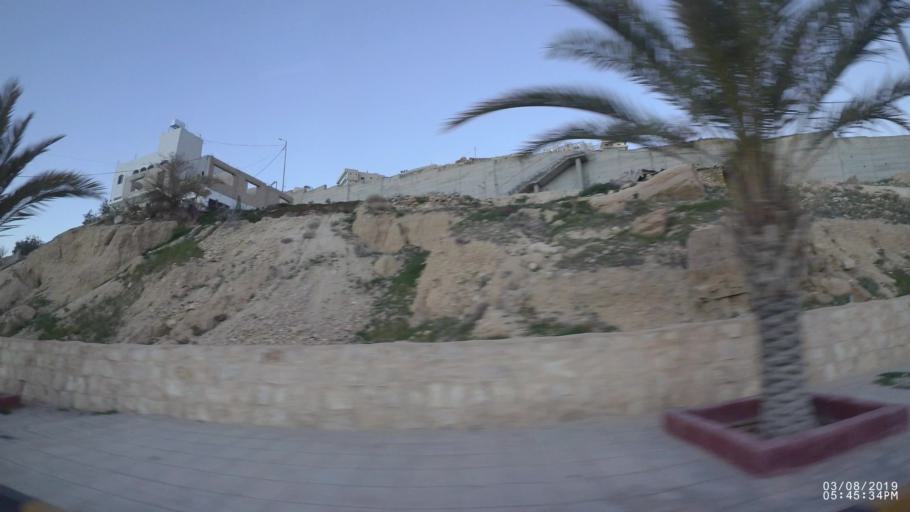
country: JO
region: Ma'an
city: Petra
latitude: 30.3148
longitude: 35.4826
